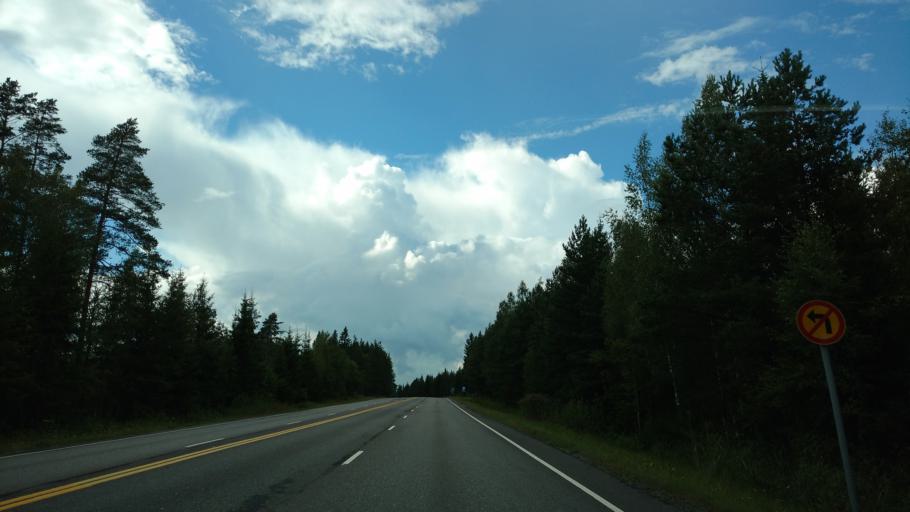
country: FI
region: Varsinais-Suomi
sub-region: Turku
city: Sauvo
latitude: 60.4026
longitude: 22.8278
